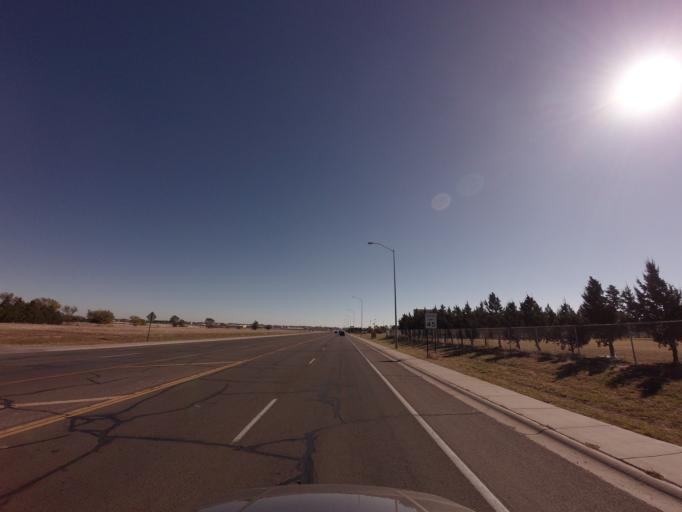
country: US
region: New Mexico
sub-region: Curry County
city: Clovis
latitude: 34.4339
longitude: -103.2128
